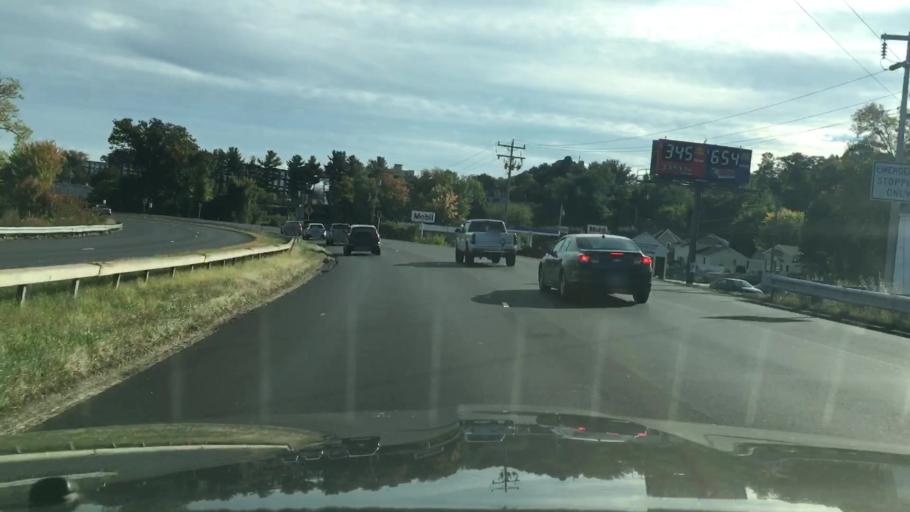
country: US
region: New Hampshire
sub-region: Hillsborough County
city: Manchester
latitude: 43.0001
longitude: -71.4751
